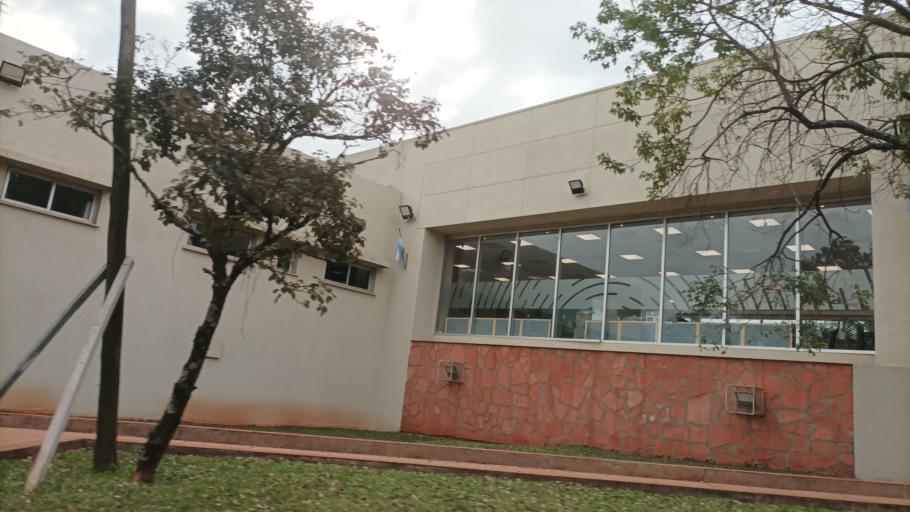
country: AR
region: Misiones
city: Aristobulo del Valle
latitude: -27.0941
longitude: -54.8907
